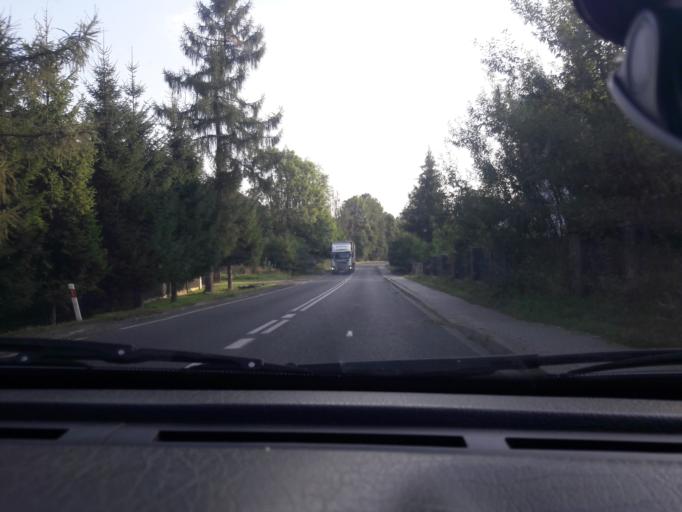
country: PL
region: Lesser Poland Voivodeship
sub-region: Powiat suski
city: Zawoja
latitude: 49.6418
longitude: 19.5383
